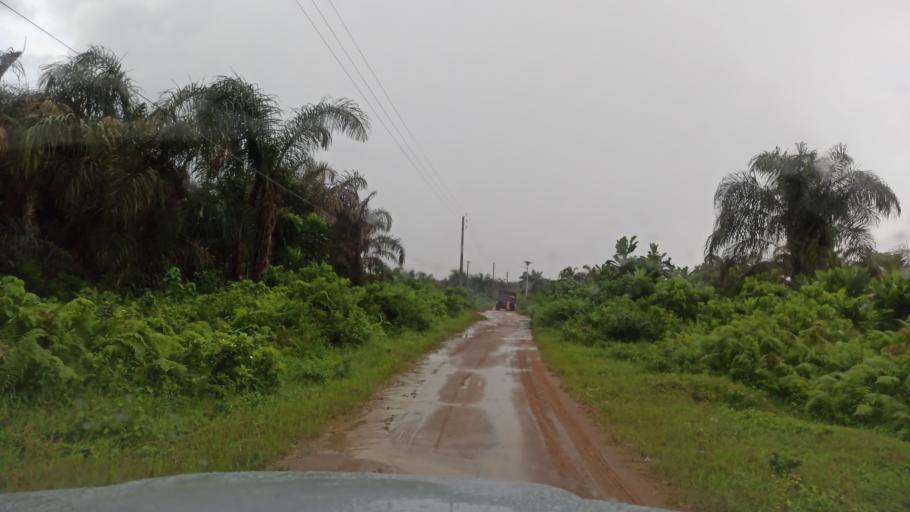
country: BJ
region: Queme
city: Porto-Novo
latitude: 6.4587
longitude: 2.6533
